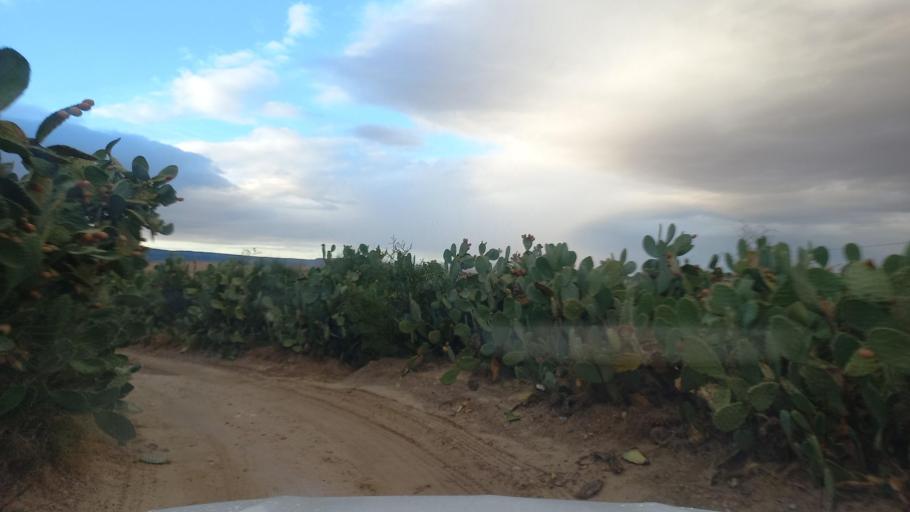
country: TN
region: Al Qasrayn
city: Kasserine
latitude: 35.2589
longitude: 8.9358
